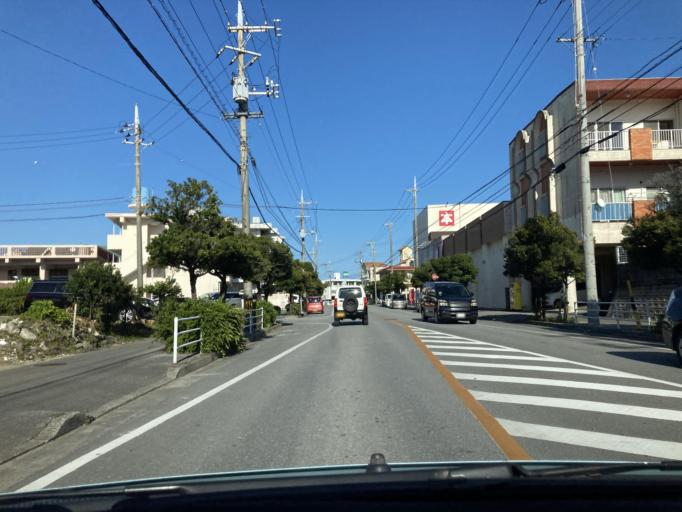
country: JP
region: Okinawa
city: Ginowan
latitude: 26.2779
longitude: 127.7789
